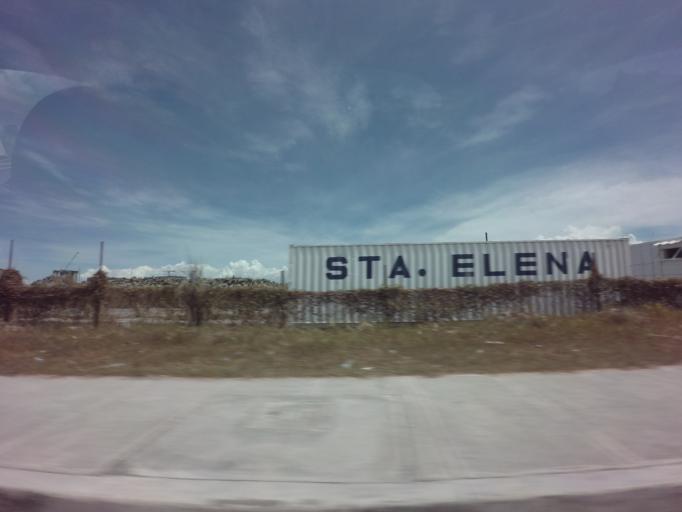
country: PH
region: Metro Manila
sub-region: Makati City
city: Makati City
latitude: 14.5174
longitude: 120.9870
